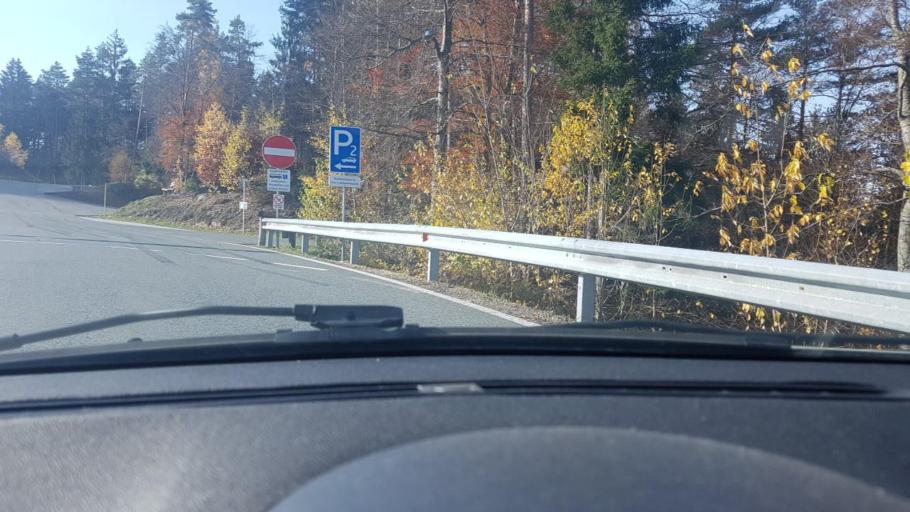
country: AT
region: Carinthia
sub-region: Politischer Bezirk Klagenfurt Land
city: Maria Worth
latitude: 46.6102
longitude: 14.1458
